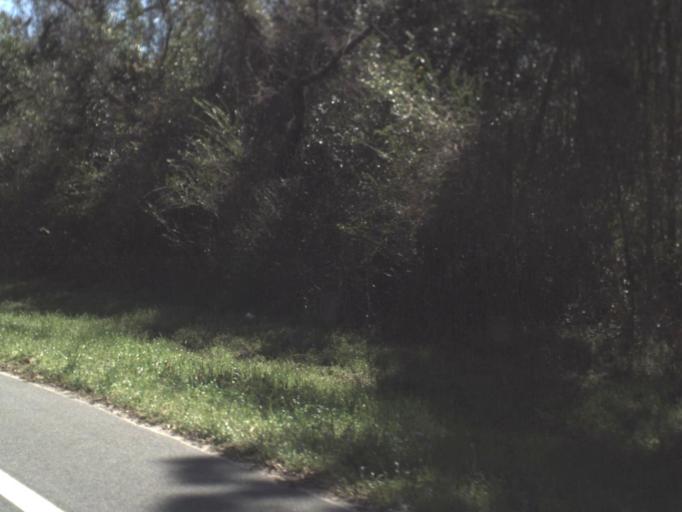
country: US
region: Florida
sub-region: Gadsden County
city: Gretna
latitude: 30.6589
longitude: -84.6923
